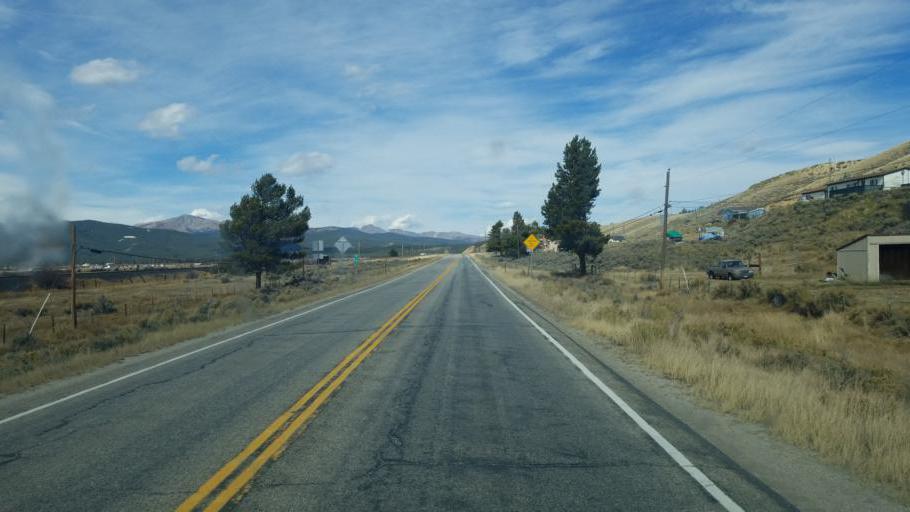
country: US
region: Colorado
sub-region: Lake County
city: Leadville North
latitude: 39.2091
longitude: -106.3456
